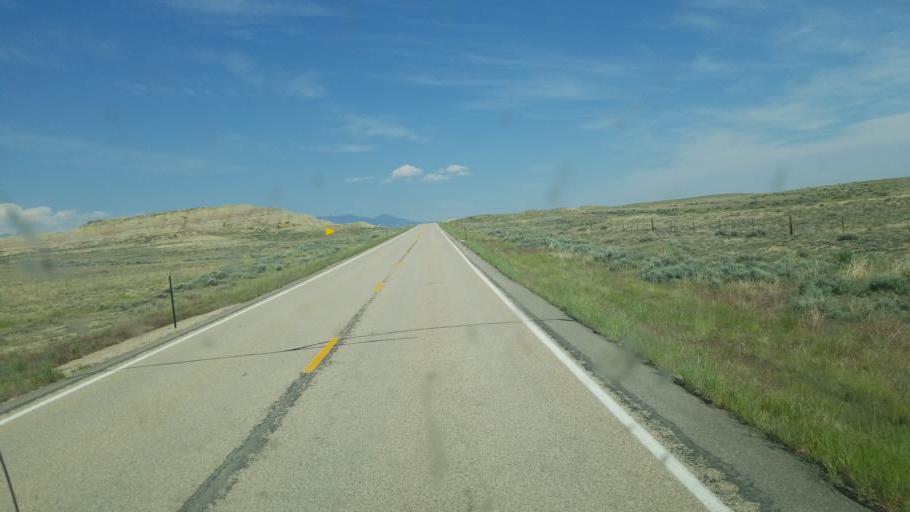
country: US
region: Wyoming
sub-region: Park County
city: Powell
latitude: 44.8368
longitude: -108.9847
